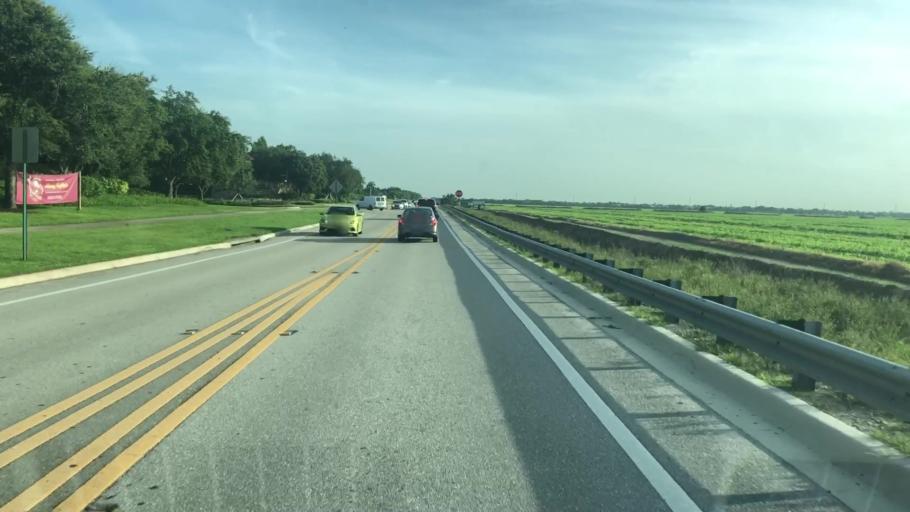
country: US
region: Florida
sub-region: Broward County
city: Parkland
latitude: 26.3223
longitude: -80.2508
